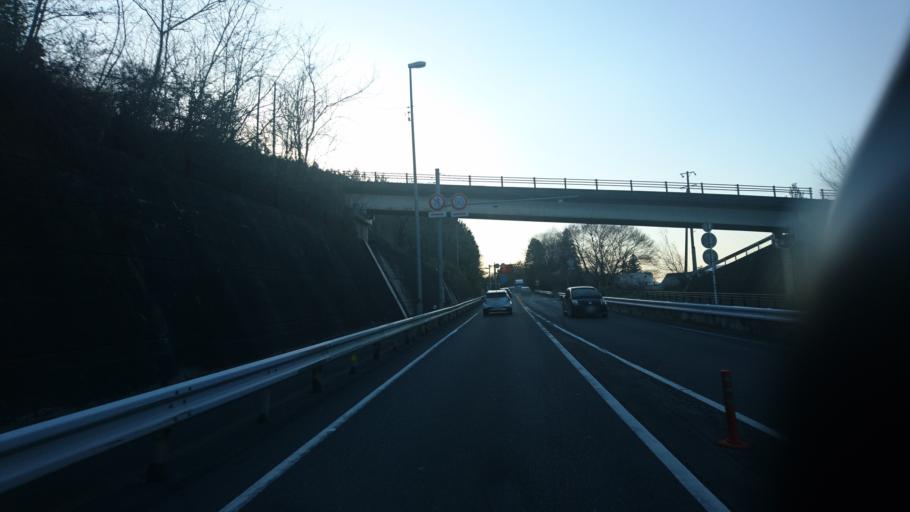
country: JP
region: Gifu
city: Nakatsugawa
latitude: 35.4462
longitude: 137.4084
